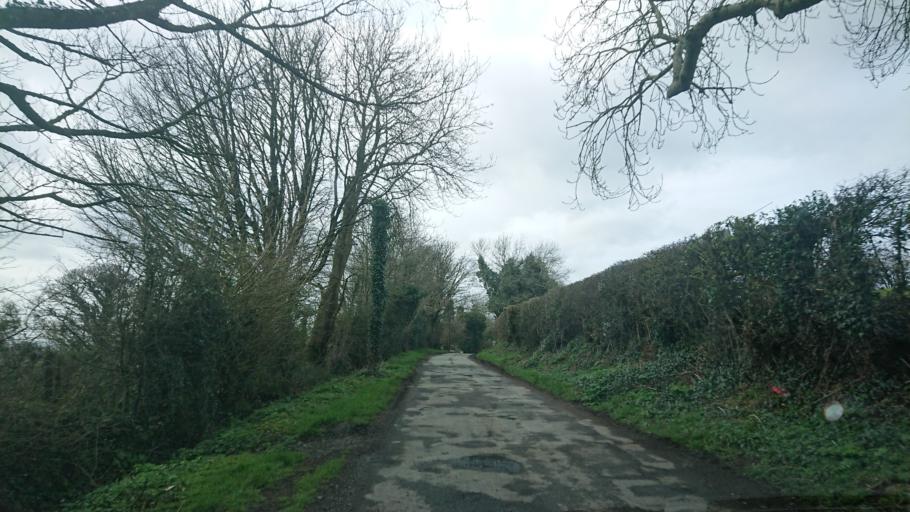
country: IE
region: Leinster
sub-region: Kildare
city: Eadestown
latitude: 53.1590
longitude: -6.5855
